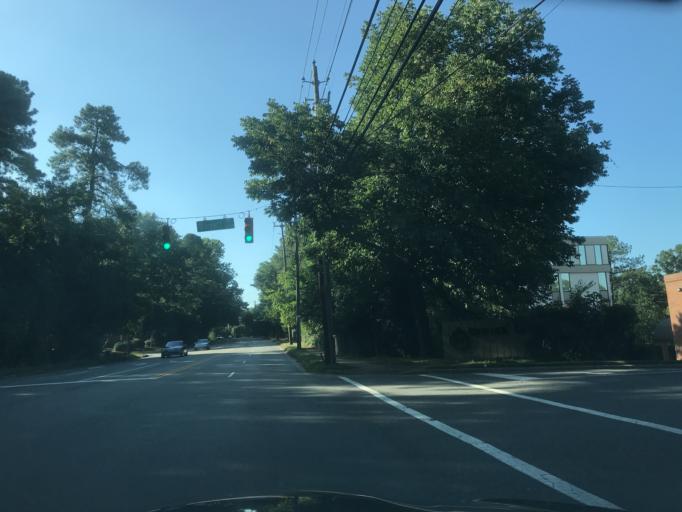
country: US
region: North Carolina
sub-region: Wake County
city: West Raleigh
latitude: 35.8276
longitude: -78.6343
